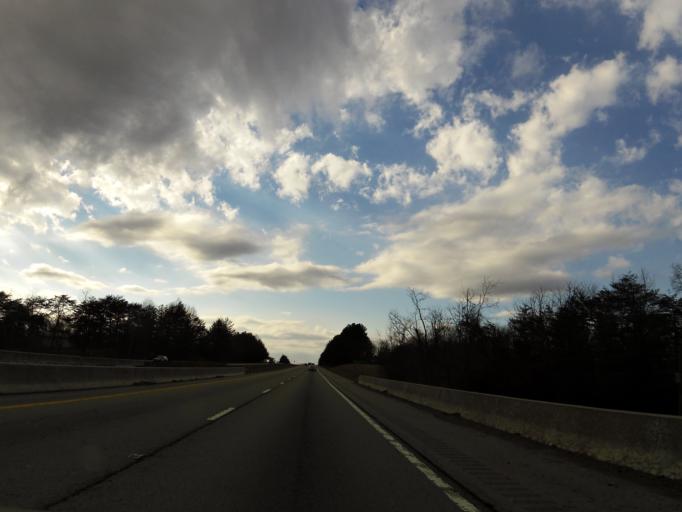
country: US
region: Tennessee
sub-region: Cumberland County
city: Fairfield Glade
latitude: 35.9132
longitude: -84.8923
